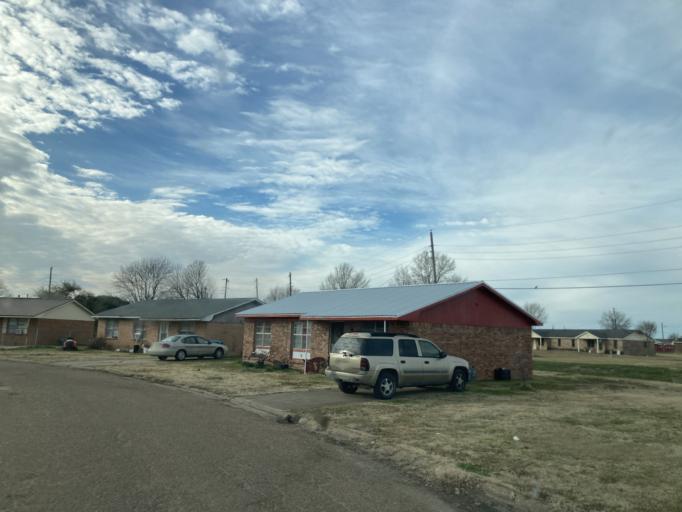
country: US
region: Mississippi
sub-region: Humphreys County
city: Belzoni
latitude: 33.1725
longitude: -90.5004
